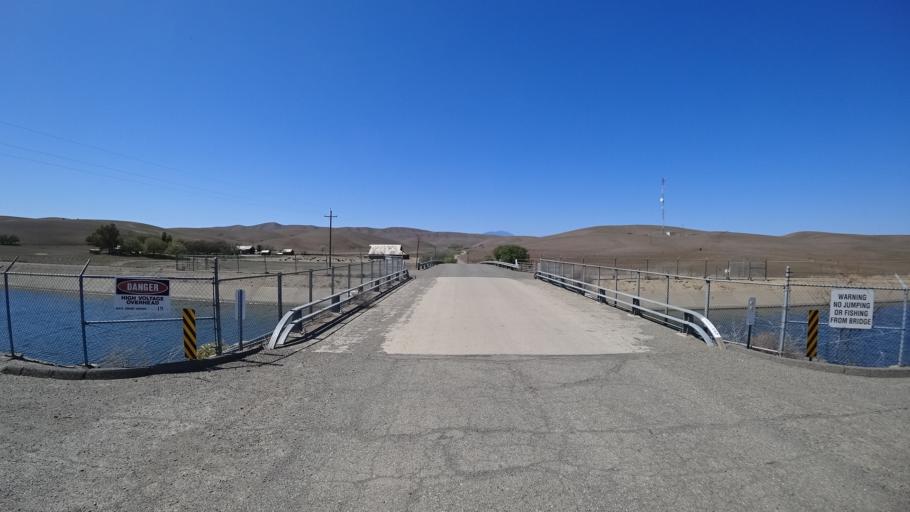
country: US
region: California
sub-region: Glenn County
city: Willows
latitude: 39.3997
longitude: -122.2878
